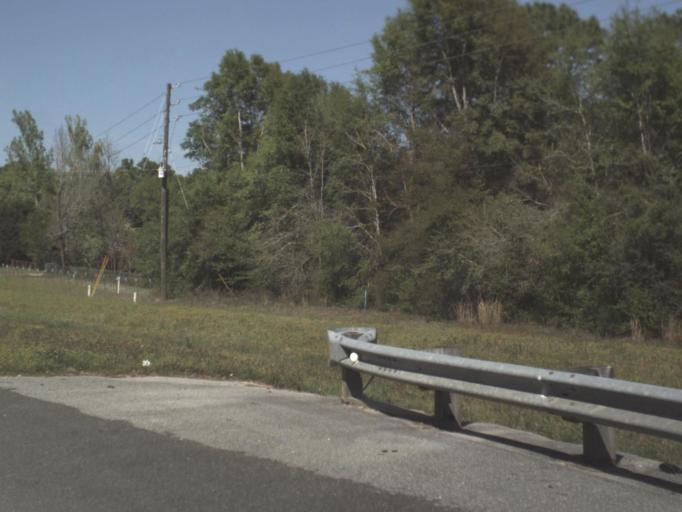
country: US
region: Florida
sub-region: Okaloosa County
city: Crestview
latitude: 30.7353
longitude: -86.6540
